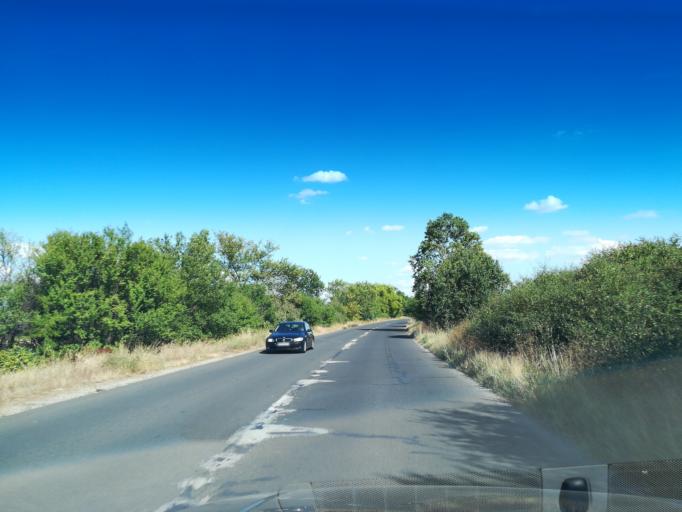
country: BG
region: Stara Zagora
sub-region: Obshtina Chirpan
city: Chirpan
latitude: 42.0709
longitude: 25.2104
